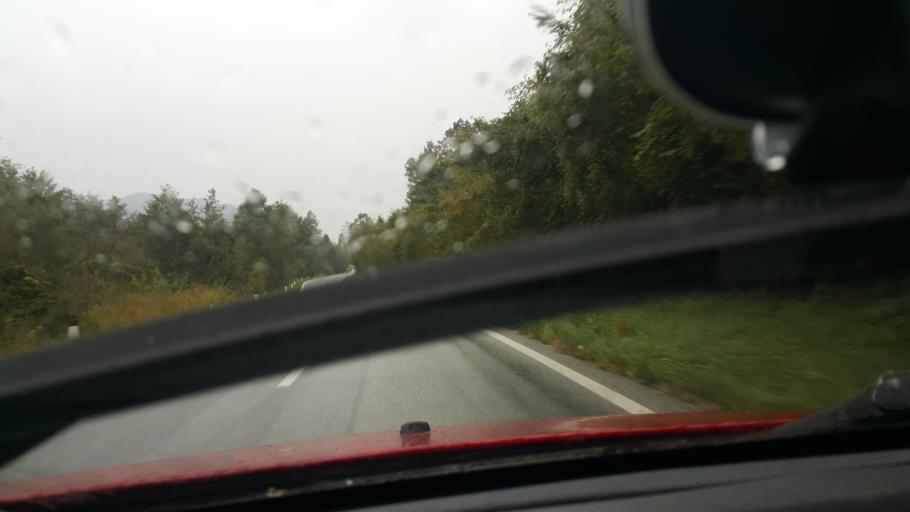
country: AT
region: Carinthia
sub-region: Politischer Bezirk Wolfsberg
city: Lavamund
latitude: 46.6549
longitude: 14.9162
